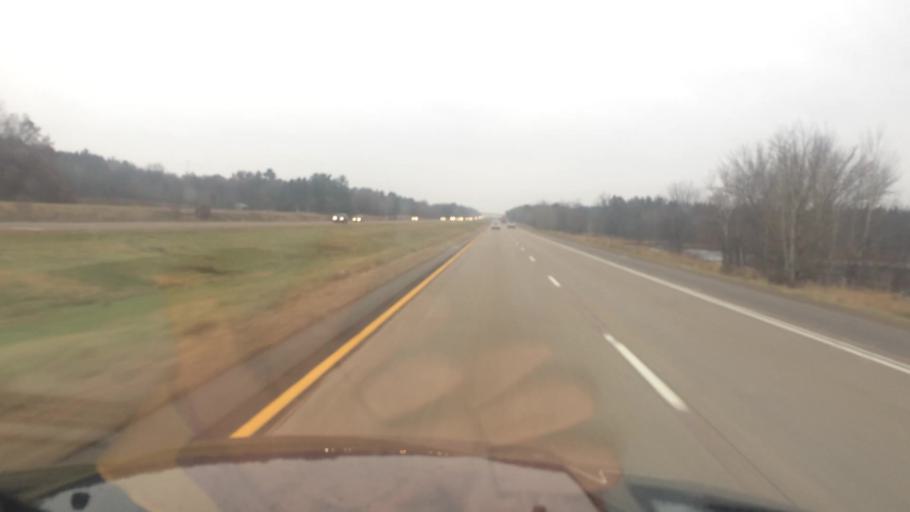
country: US
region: Wisconsin
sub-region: Portage County
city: Stevens Point
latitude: 44.6143
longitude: -89.6251
